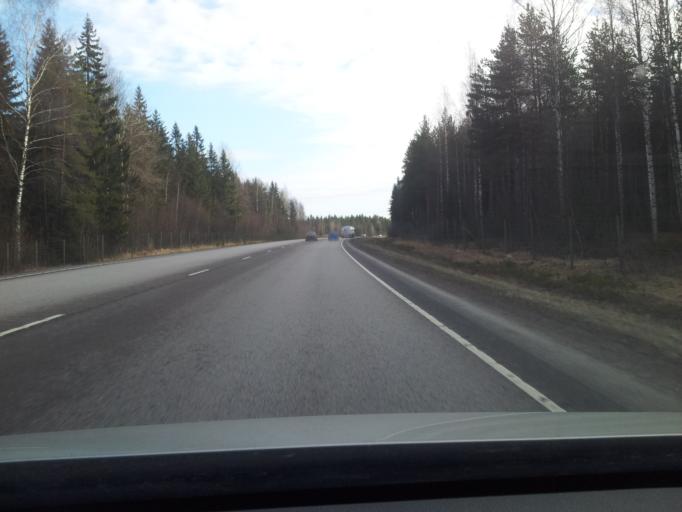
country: FI
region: Uusimaa
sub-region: Loviisa
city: Lapinjaervi
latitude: 60.6782
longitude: 26.2563
